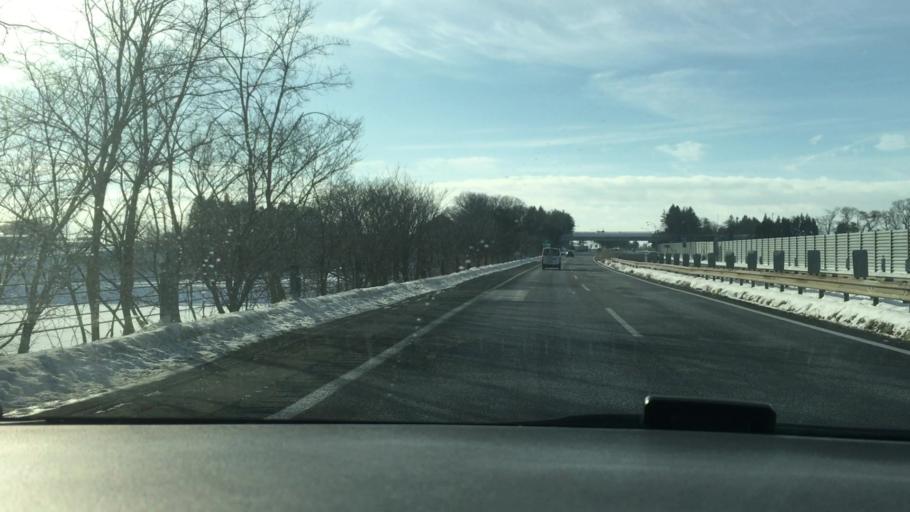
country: JP
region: Iwate
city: Hanamaki
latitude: 39.3746
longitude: 141.0931
